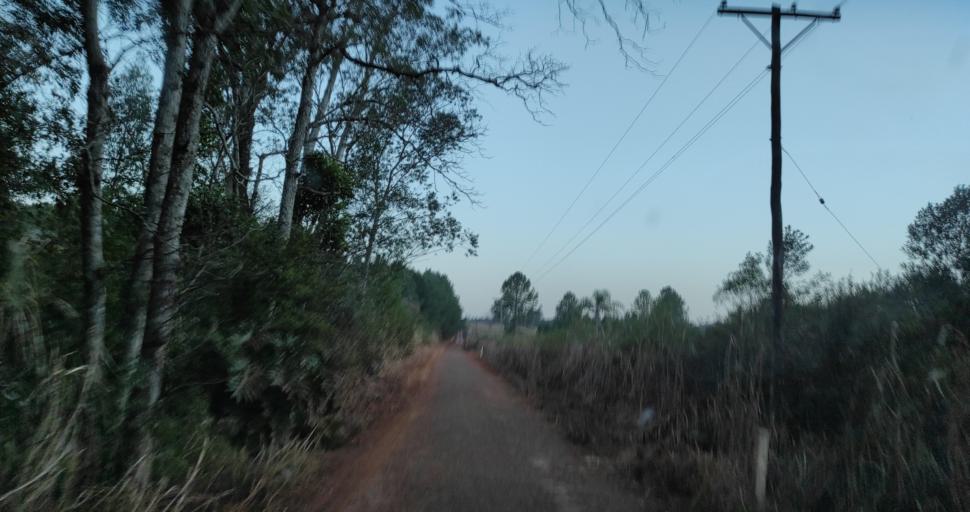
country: AR
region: Misiones
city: Capiovi
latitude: -26.8970
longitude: -55.0496
